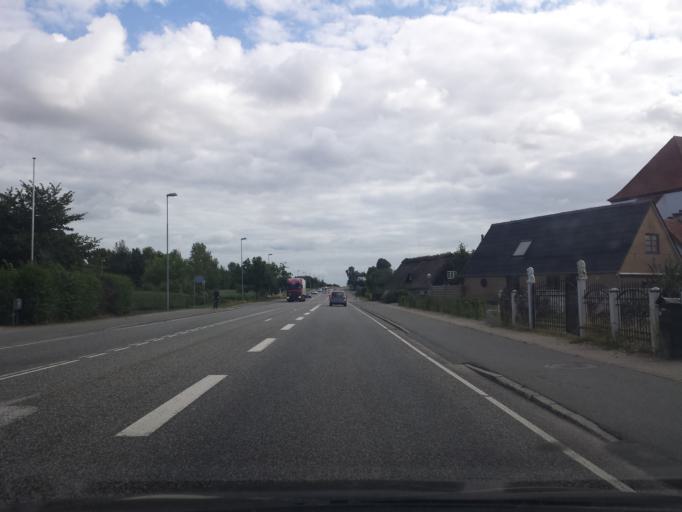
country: DK
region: South Denmark
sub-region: Sonderborg Kommune
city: Augustenborg
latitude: 54.9677
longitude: 9.8990
